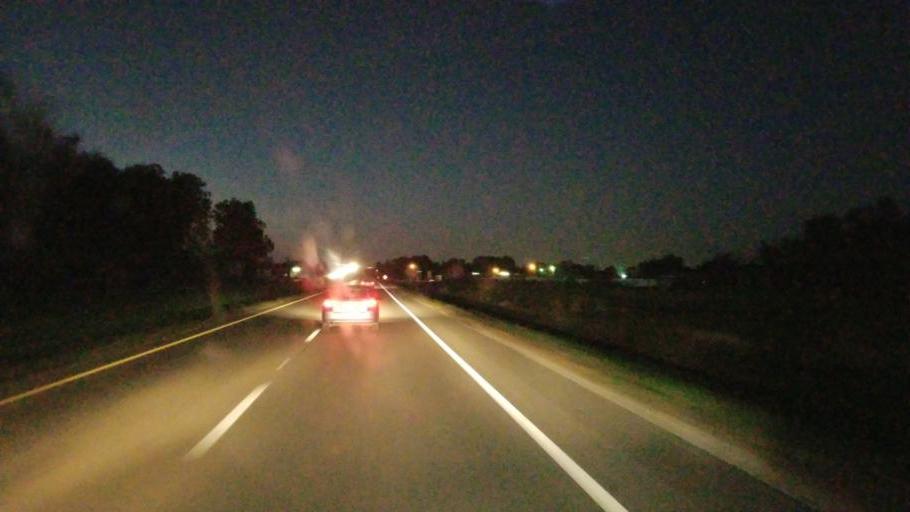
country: US
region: Ohio
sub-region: Pickaway County
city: Circleville
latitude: 39.6179
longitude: -82.9498
